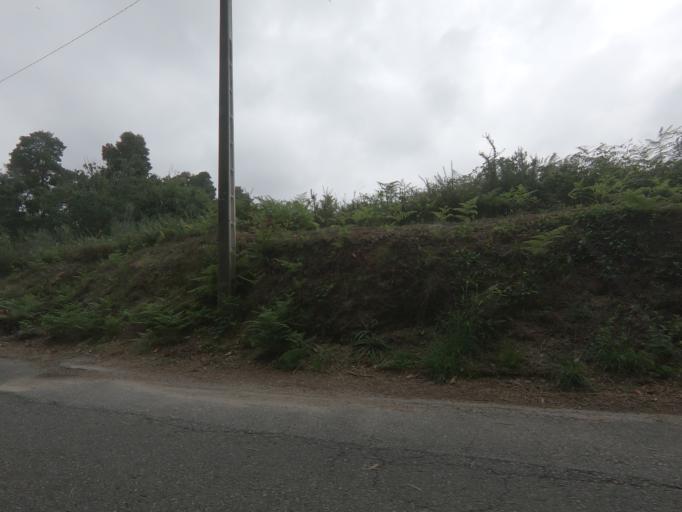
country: ES
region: Galicia
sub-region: Provincia de Pontevedra
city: Tui
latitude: 42.0470
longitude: -8.6564
